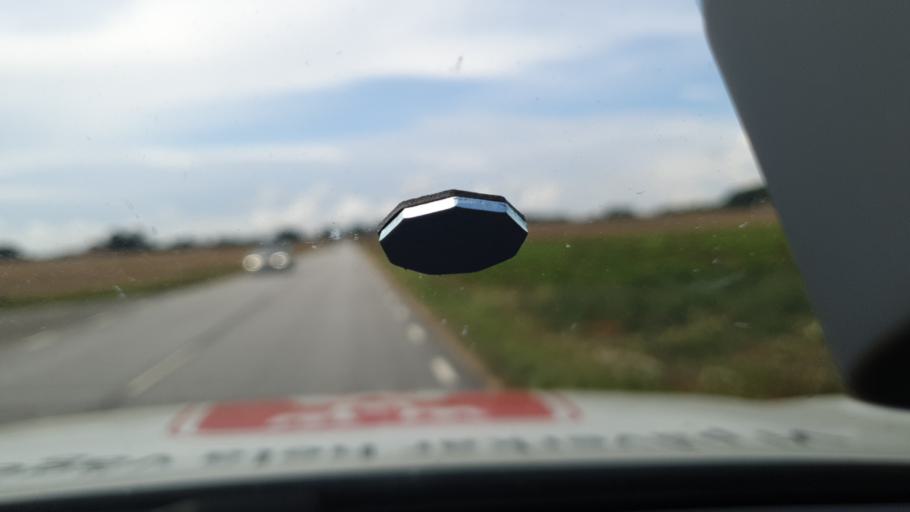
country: SE
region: Skane
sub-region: Simrishamns Kommun
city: Simrishamn
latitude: 55.4648
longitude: 14.2001
